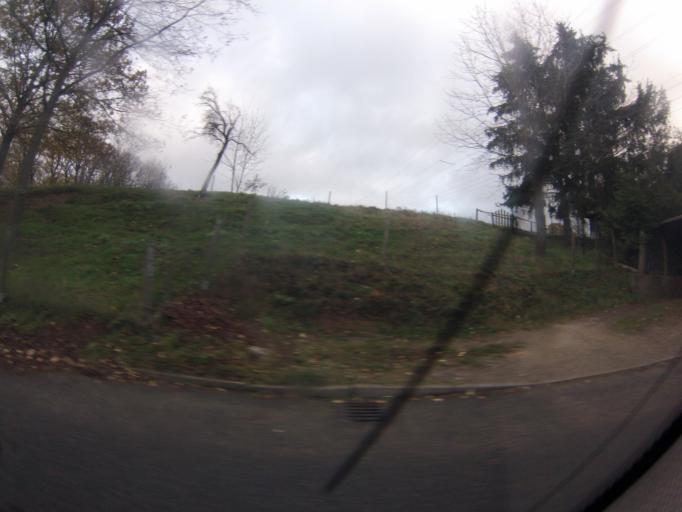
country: DE
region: Thuringia
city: Nobdenitz
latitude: 50.8568
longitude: 12.2828
